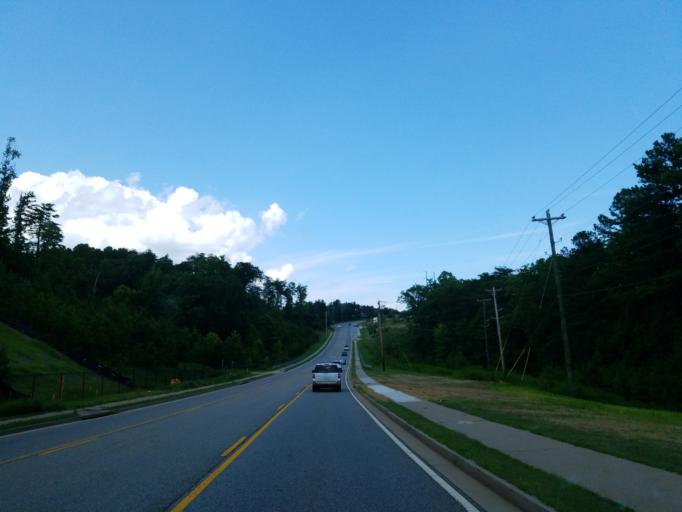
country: US
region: Georgia
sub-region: Forsyth County
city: Cumming
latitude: 34.2238
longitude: -84.1162
